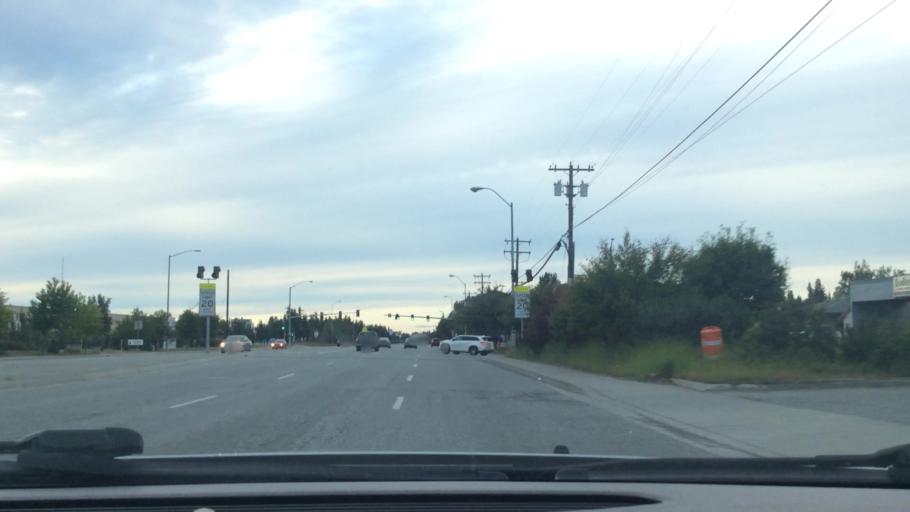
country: US
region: Alaska
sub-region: Anchorage Municipality
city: Anchorage
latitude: 61.1957
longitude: -149.9128
